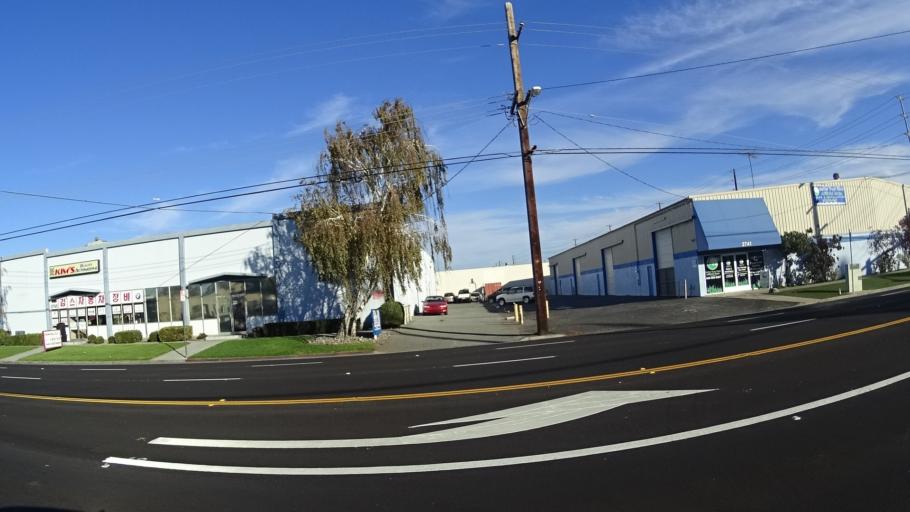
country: US
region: California
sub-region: Santa Clara County
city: Santa Clara
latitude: 37.3701
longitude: -121.9596
